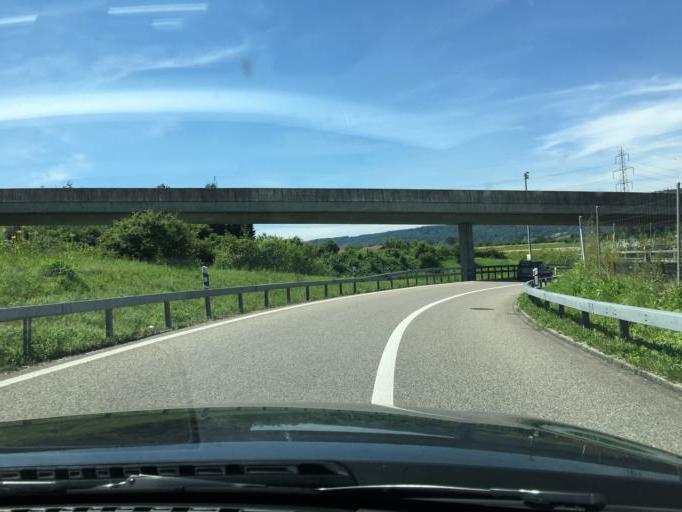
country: CH
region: Basel-Landschaft
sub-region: Bezirk Liestal
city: Arisdorf
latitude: 47.5413
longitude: 7.7607
